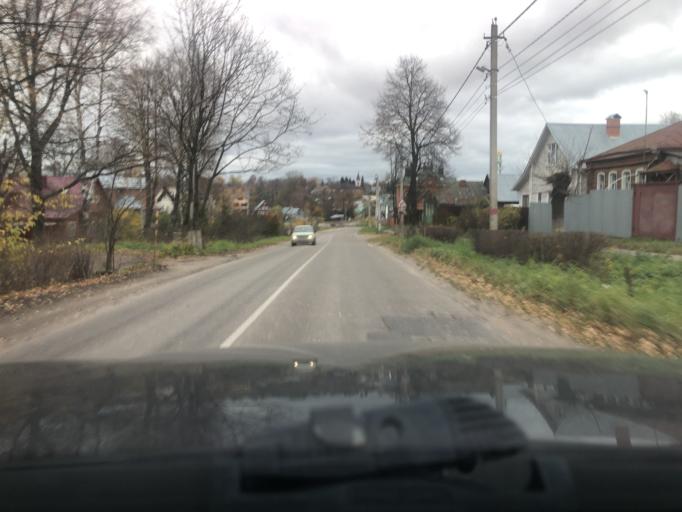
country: RU
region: Moskovskaya
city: Sergiyev Posad
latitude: 56.3013
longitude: 38.1239
